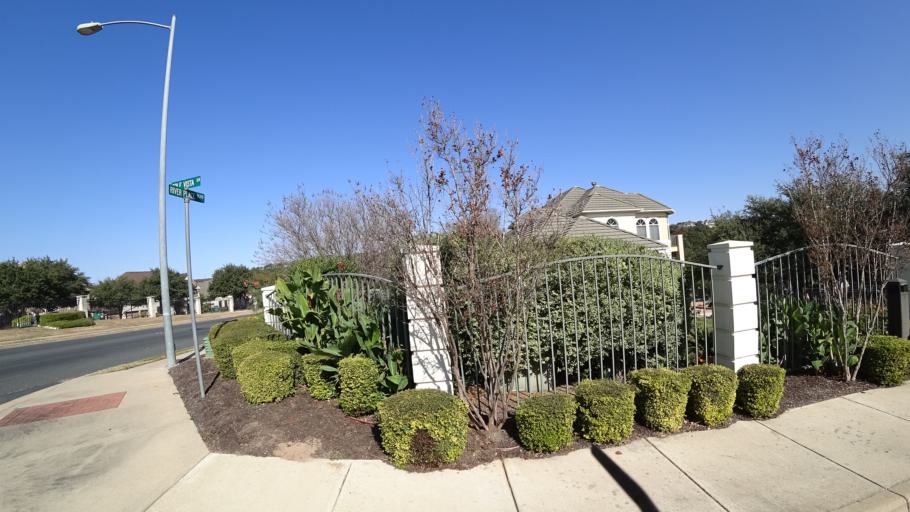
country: US
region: Texas
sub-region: Travis County
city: Lost Creek
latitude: 30.3722
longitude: -97.8570
